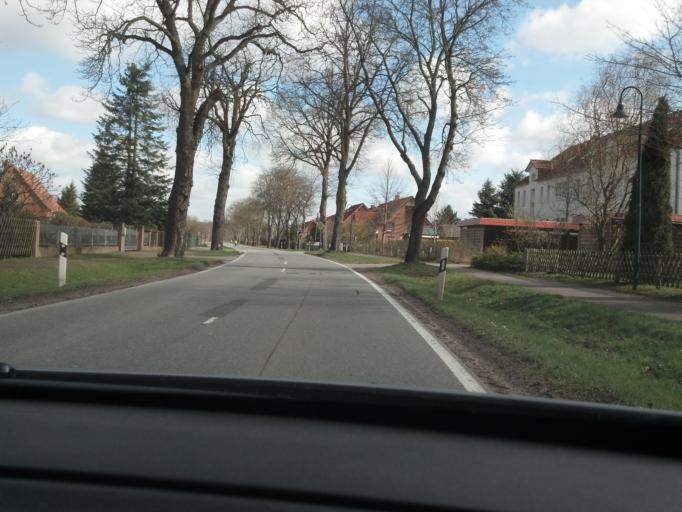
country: DE
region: Mecklenburg-Vorpommern
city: Boizenburg
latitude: 53.4323
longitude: 10.7476
